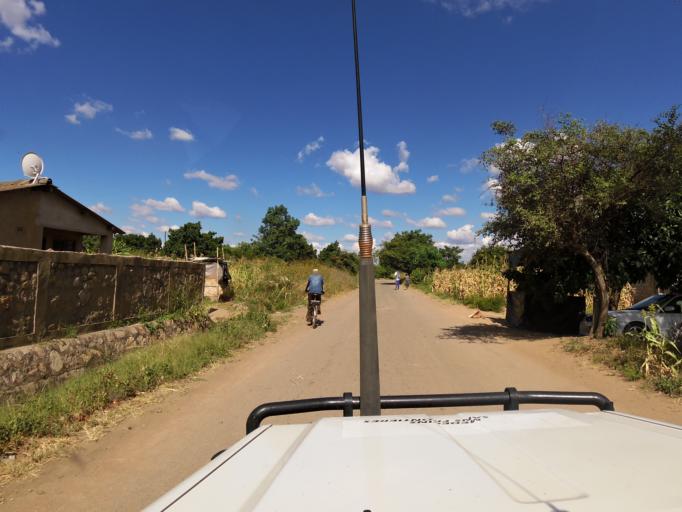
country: ZW
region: Harare
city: Epworth
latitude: -17.8703
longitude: 31.1355
